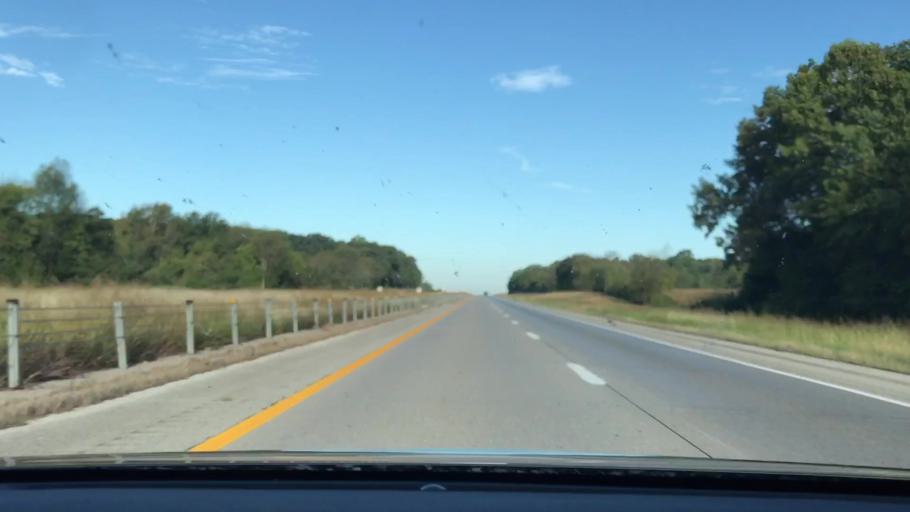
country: US
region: Kentucky
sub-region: Christian County
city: Hopkinsville
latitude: 36.7741
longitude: -87.5620
